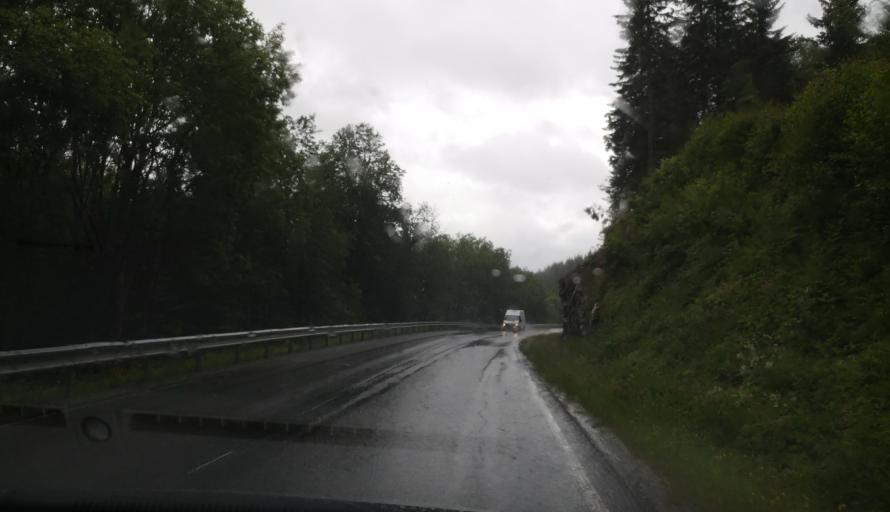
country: NO
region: Sor-Trondelag
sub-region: Selbu
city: Mebonden
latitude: 63.3078
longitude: 11.0793
